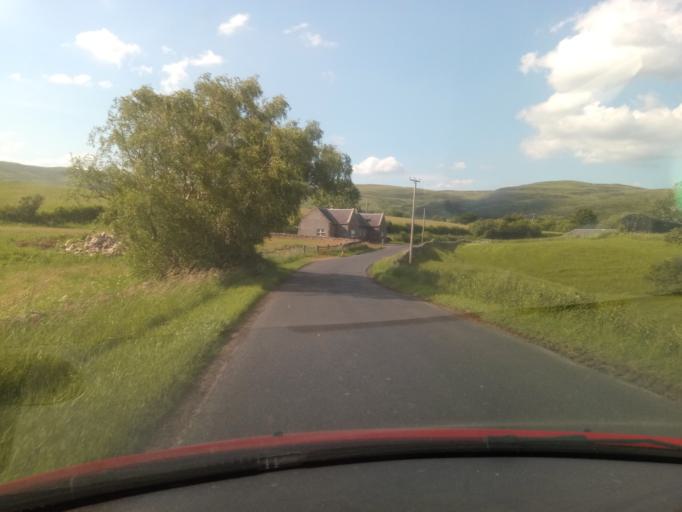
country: GB
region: Scotland
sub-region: The Scottish Borders
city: Innerleithen
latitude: 55.5021
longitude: -2.9835
